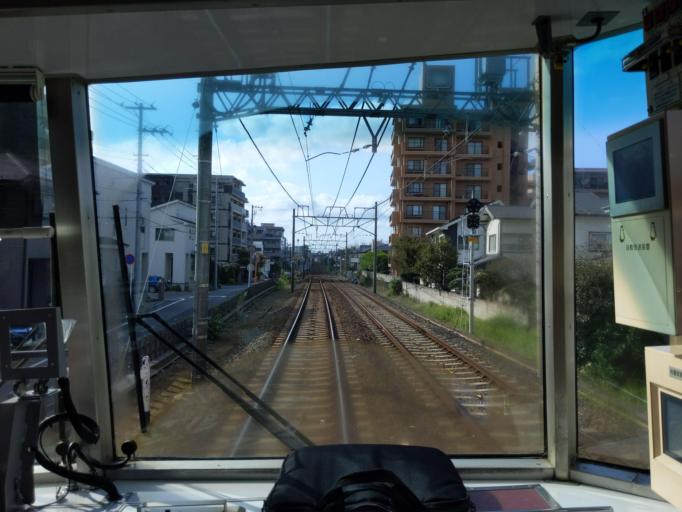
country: JP
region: Chiba
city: Kashiwa
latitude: 35.8024
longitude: 139.9605
